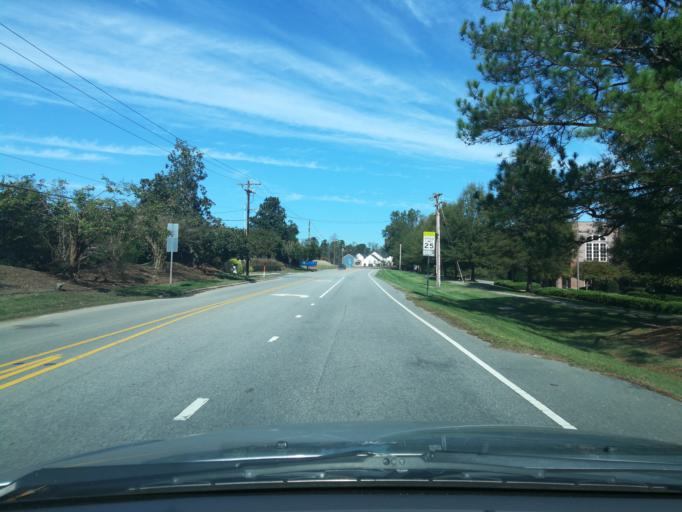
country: US
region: North Carolina
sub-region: Durham County
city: Durham
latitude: 35.9692
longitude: -78.9768
